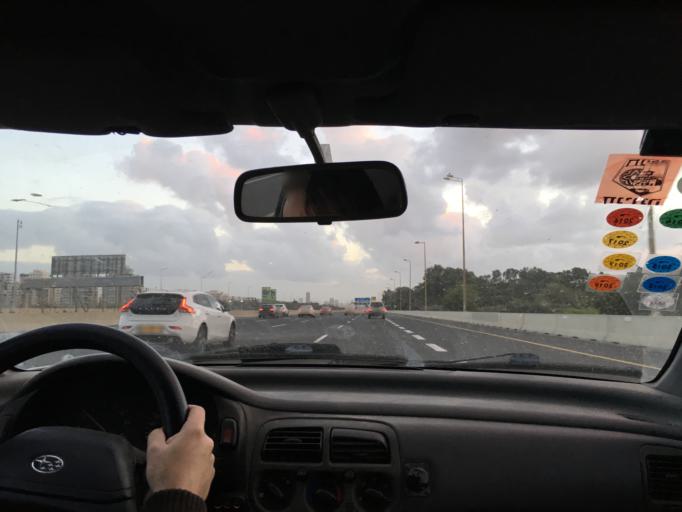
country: IL
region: Tel Aviv
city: Ramat HaSharon
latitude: 32.1308
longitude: 34.8098
